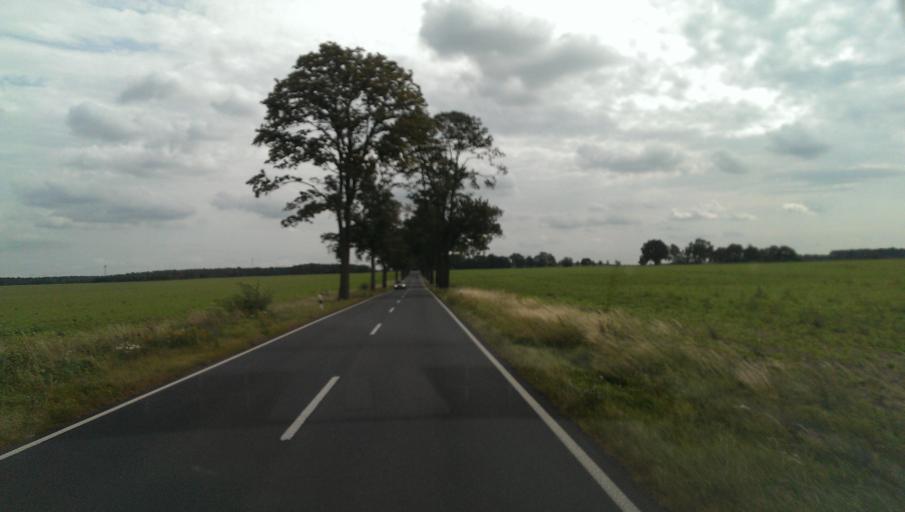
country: DE
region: Brandenburg
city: Am Mellensee
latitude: 52.2300
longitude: 13.3222
